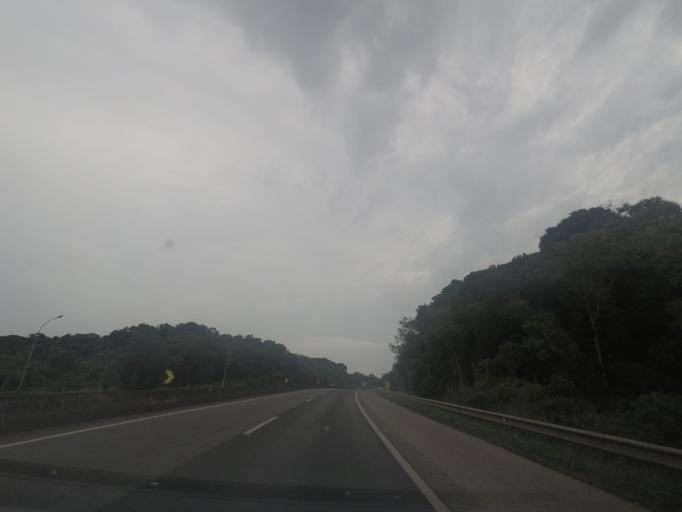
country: BR
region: Sao Paulo
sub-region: Pariquera-Acu
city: Pariquera Acu
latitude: -24.6032
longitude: -47.8768
